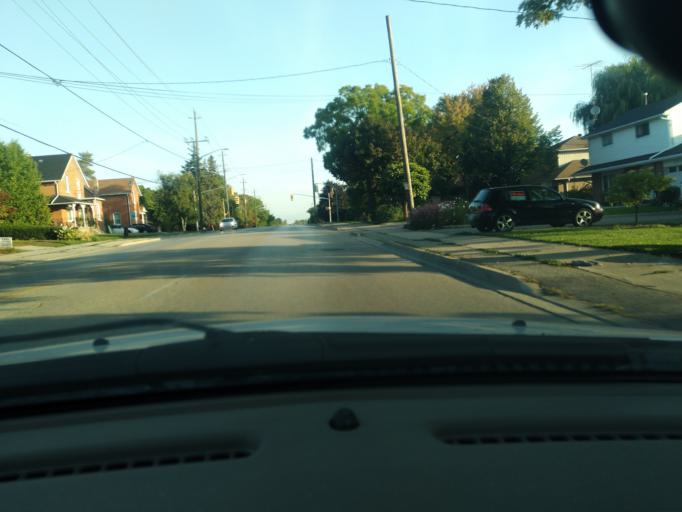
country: CA
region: Ontario
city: Bradford West Gwillimbury
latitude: 44.1198
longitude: -79.5662
